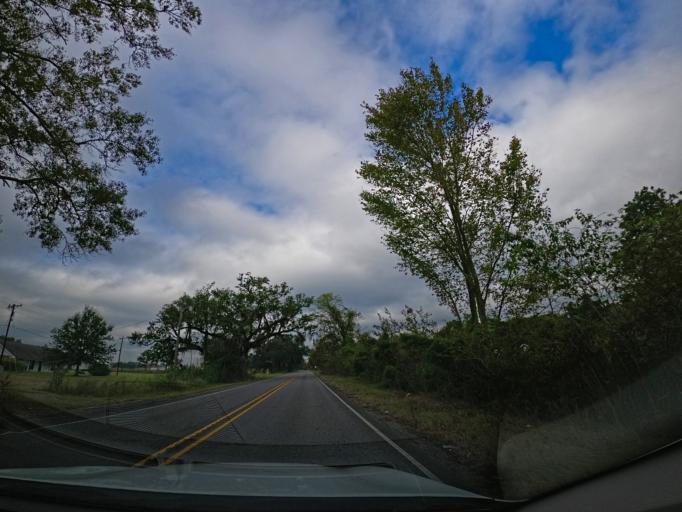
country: US
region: Louisiana
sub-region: Terrebonne Parish
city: Gray
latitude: 29.6309
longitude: -90.9281
